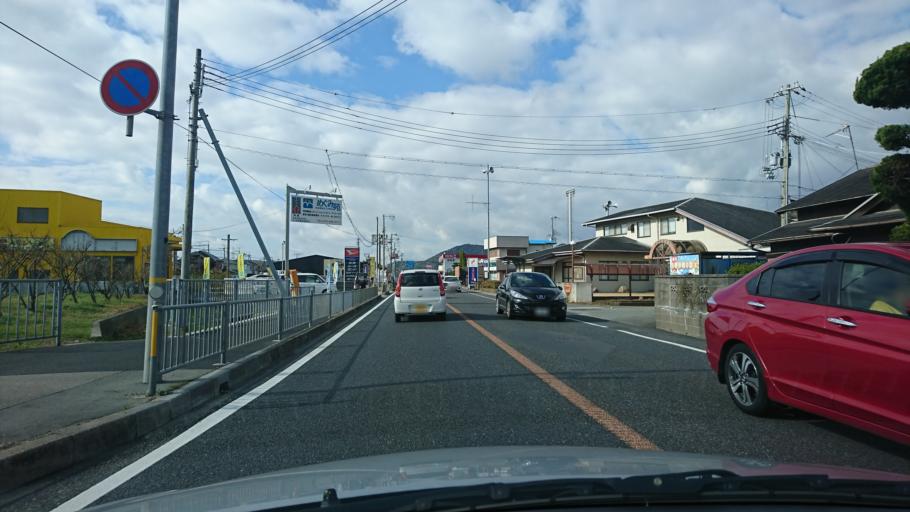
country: JP
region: Hyogo
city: Kakogawacho-honmachi
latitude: 34.7912
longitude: 134.7962
